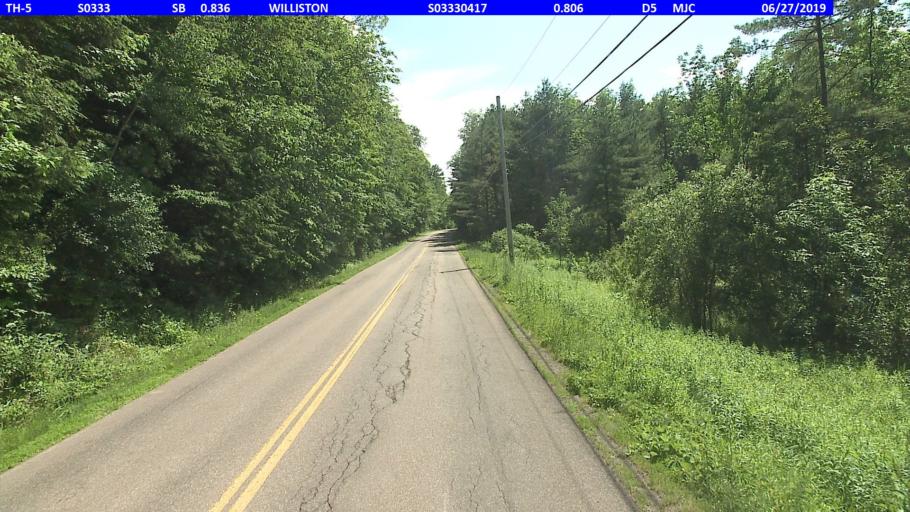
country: US
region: Vermont
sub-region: Chittenden County
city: South Burlington
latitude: 44.4130
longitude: -73.1388
